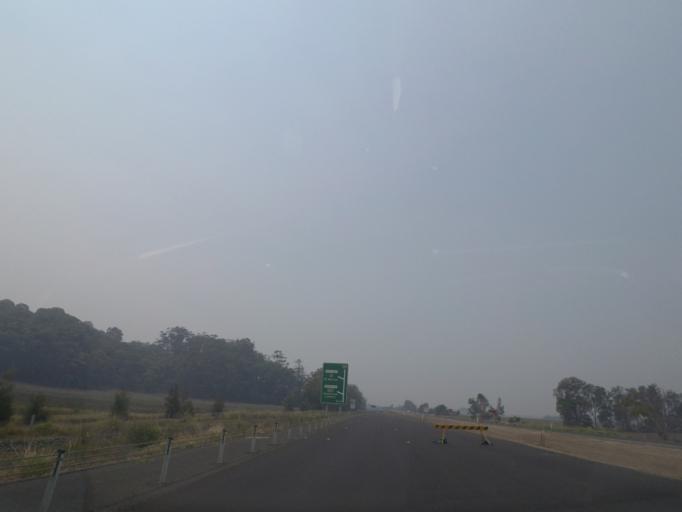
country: AU
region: New South Wales
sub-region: Ballina
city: Ballina
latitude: -28.8822
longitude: 153.4850
